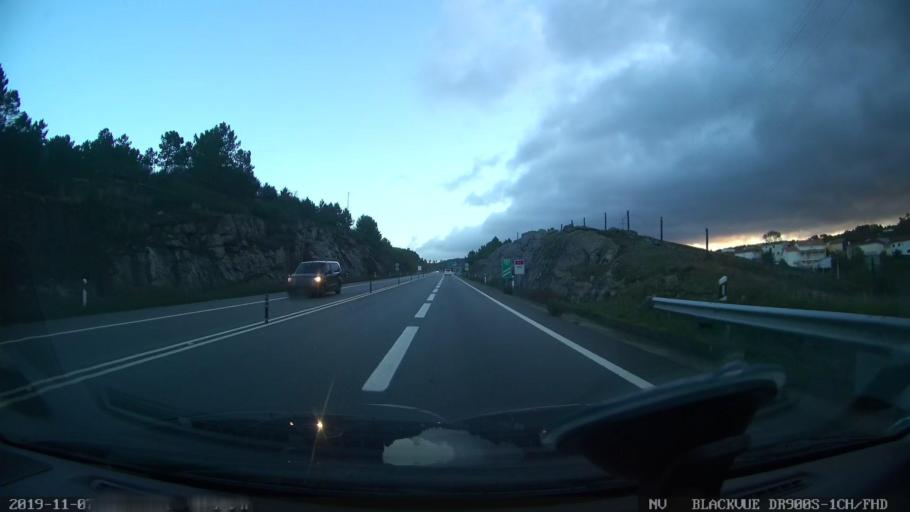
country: PT
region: Vila Real
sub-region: Vila Real
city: Vila Real
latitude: 41.3181
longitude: -7.7038
